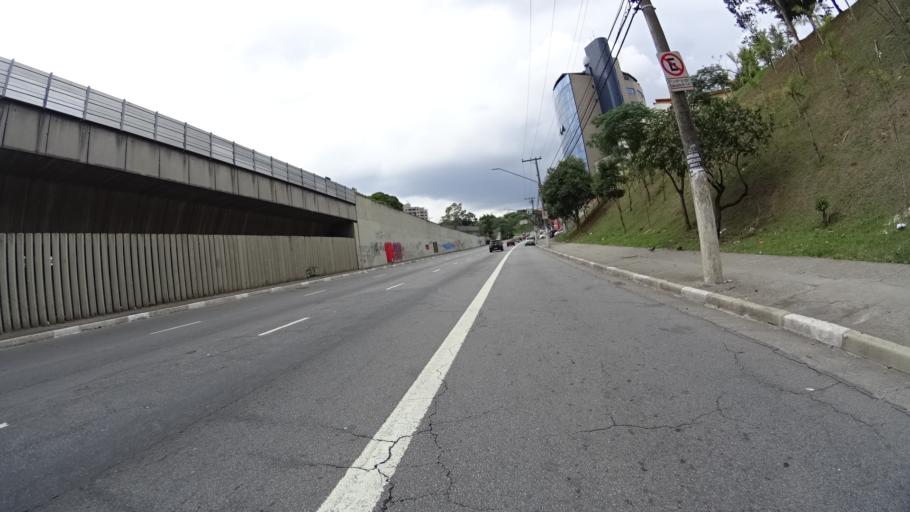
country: BR
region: Sao Paulo
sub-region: Sao Paulo
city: Sao Paulo
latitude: -23.4855
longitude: -46.6079
